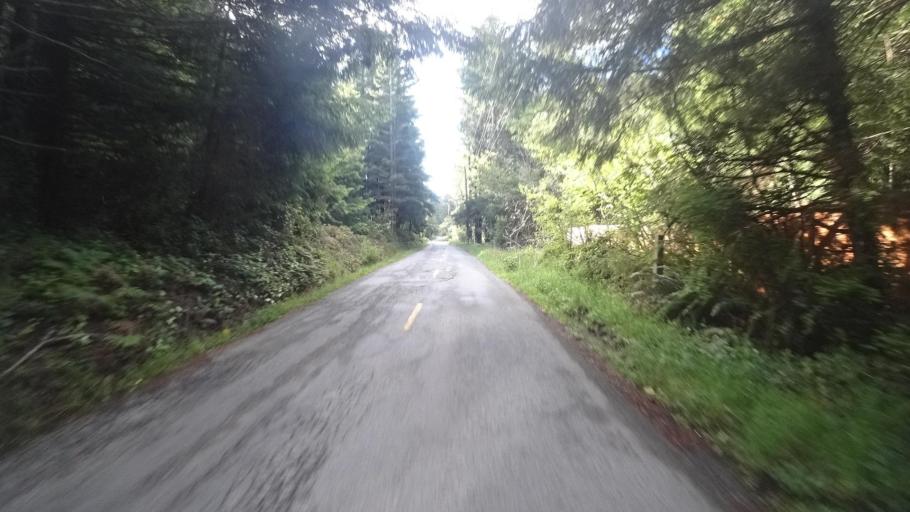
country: US
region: California
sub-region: Humboldt County
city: Westhaven-Moonstone
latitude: 41.0532
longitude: -124.1223
